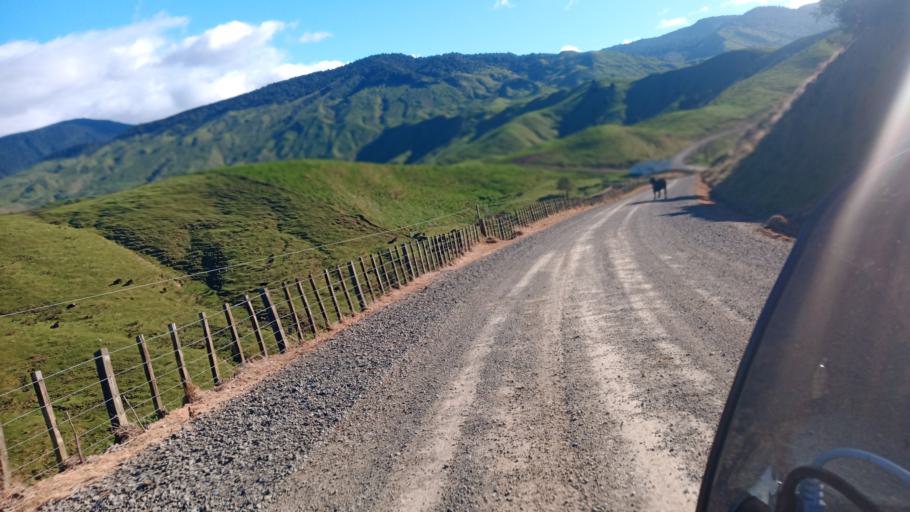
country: NZ
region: Hawke's Bay
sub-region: Wairoa District
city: Wairoa
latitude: -38.7814
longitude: 177.2647
